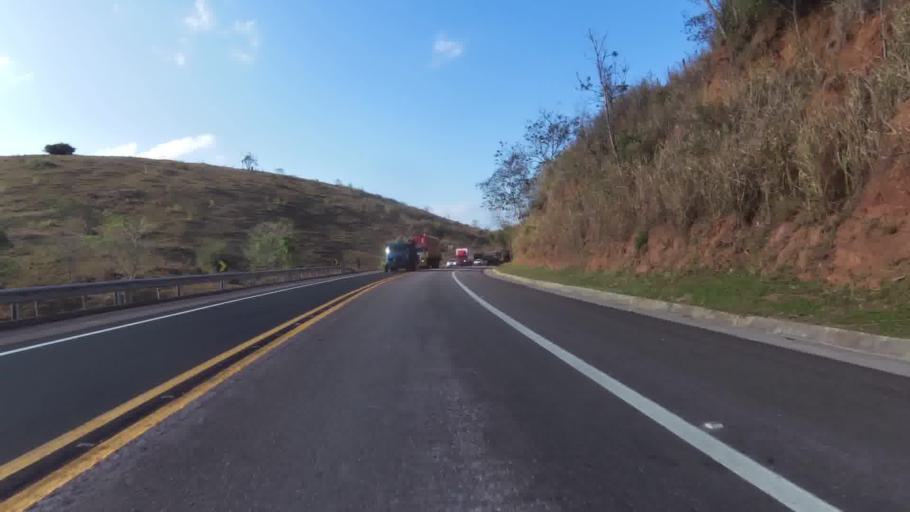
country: BR
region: Espirito Santo
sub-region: Mimoso Do Sul
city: Mimoso do Sul
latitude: -21.2301
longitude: -41.3168
